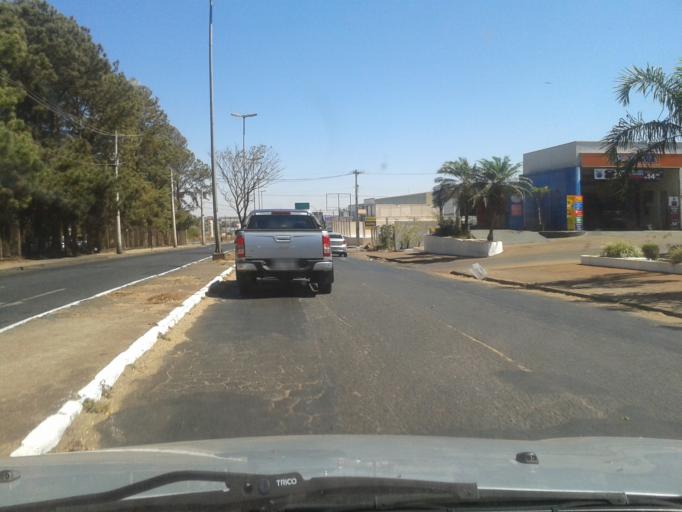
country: BR
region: Minas Gerais
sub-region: Uberlandia
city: Uberlandia
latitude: -18.8824
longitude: -48.2689
